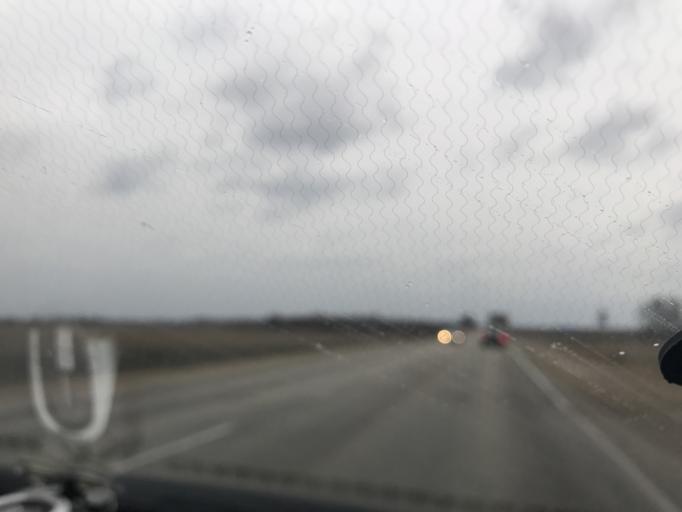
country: RU
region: Krasnodarskiy
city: Novoleushkovskaya
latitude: 45.9983
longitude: 40.0235
